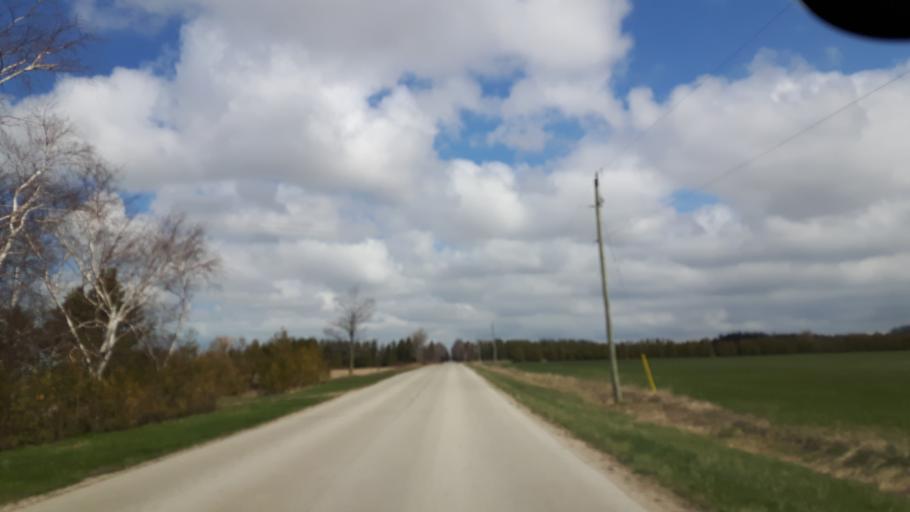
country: CA
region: Ontario
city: Goderich
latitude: 43.6474
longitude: -81.6846
